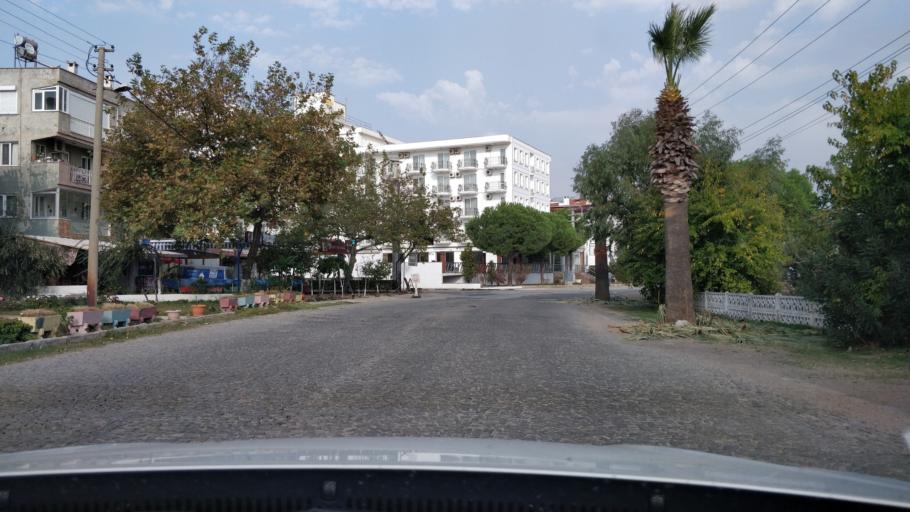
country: TR
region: Balikesir
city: Ayvalik
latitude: 39.2693
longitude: 26.6495
